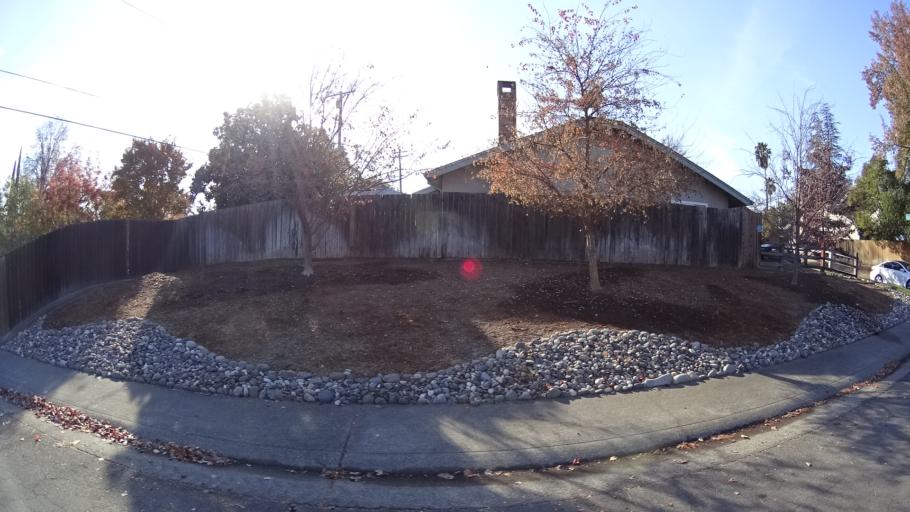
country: US
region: California
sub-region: Sacramento County
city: Antelope
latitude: 38.6803
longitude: -121.3087
